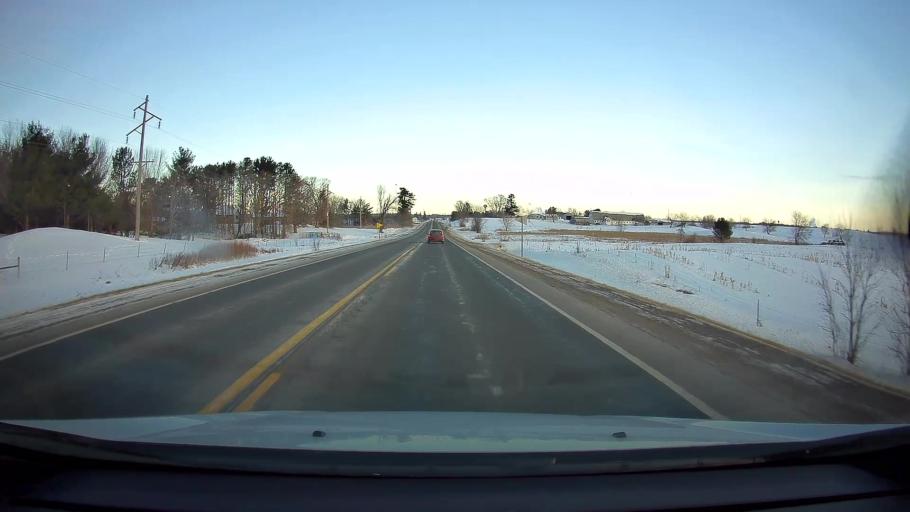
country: US
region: Wisconsin
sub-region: Barron County
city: Turtle Lake
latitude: 45.3764
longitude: -92.1667
